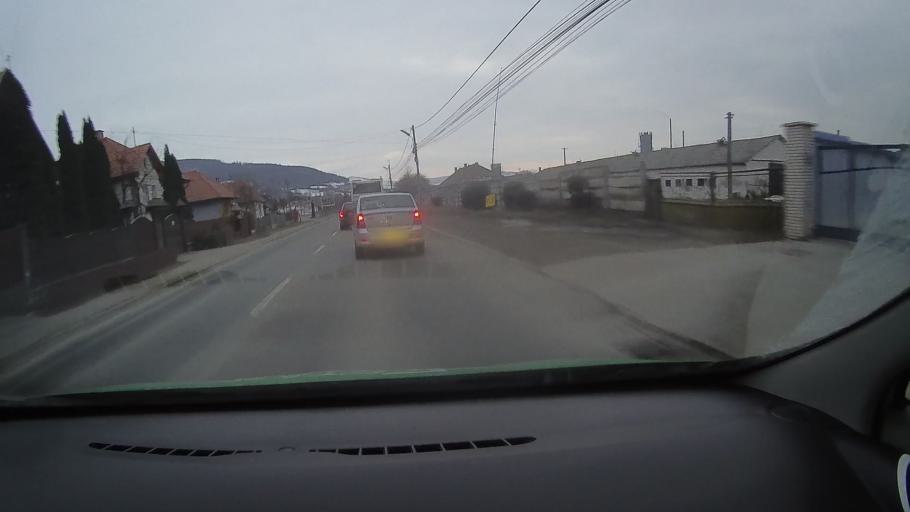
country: RO
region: Harghita
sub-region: Municipiul Odorheiu Secuiesc
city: Odorheiu Secuiesc
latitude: 46.2890
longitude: 25.2900
